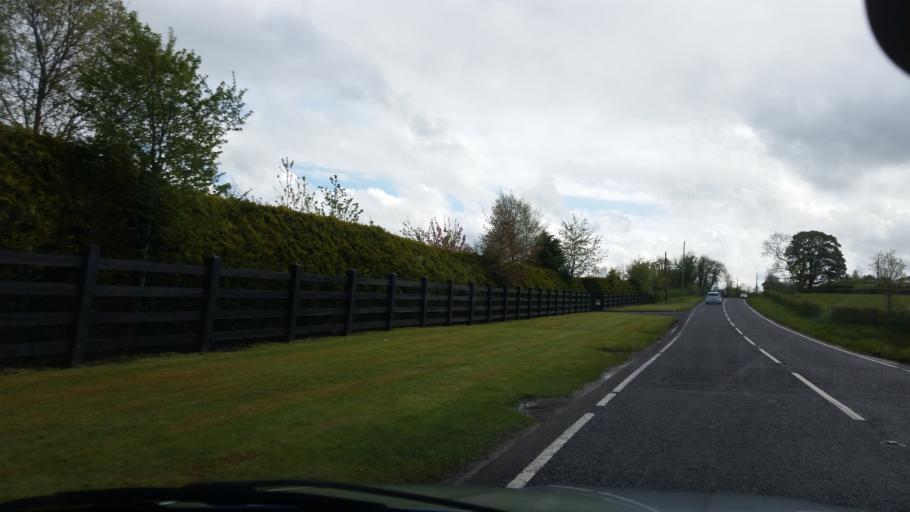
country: GB
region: Northern Ireland
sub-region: Omagh District
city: Omagh
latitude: 54.5596
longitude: -7.2778
